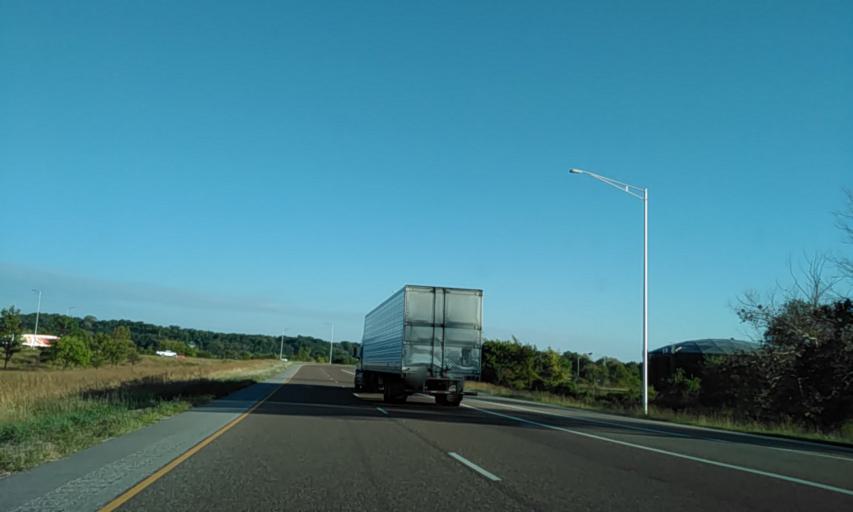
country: US
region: Illinois
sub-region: Saint Clair County
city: Caseyville
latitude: 38.6699
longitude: -90.0321
